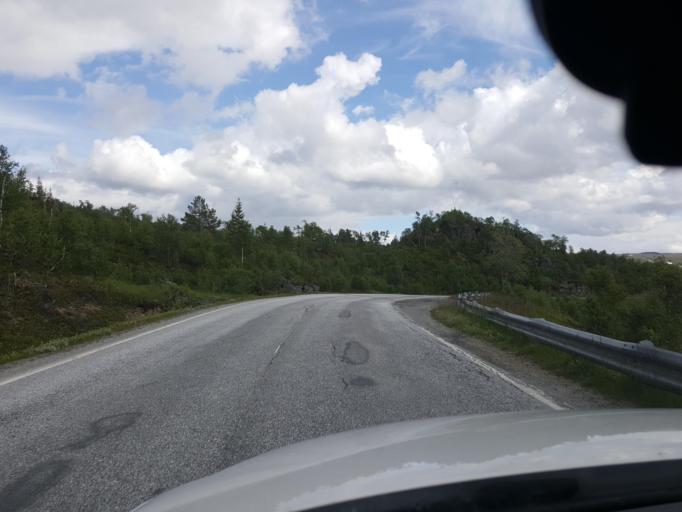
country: NO
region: Nordland
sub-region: Rana
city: Mo i Rana
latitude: 66.2863
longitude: 14.4503
